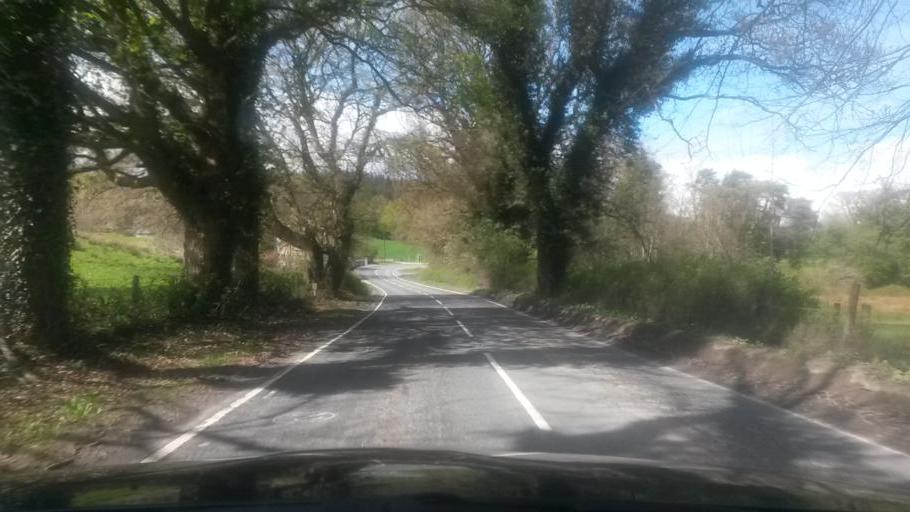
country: GB
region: Northern Ireland
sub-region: Fermanagh District
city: Enniskillen
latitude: 54.3732
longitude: -7.6867
